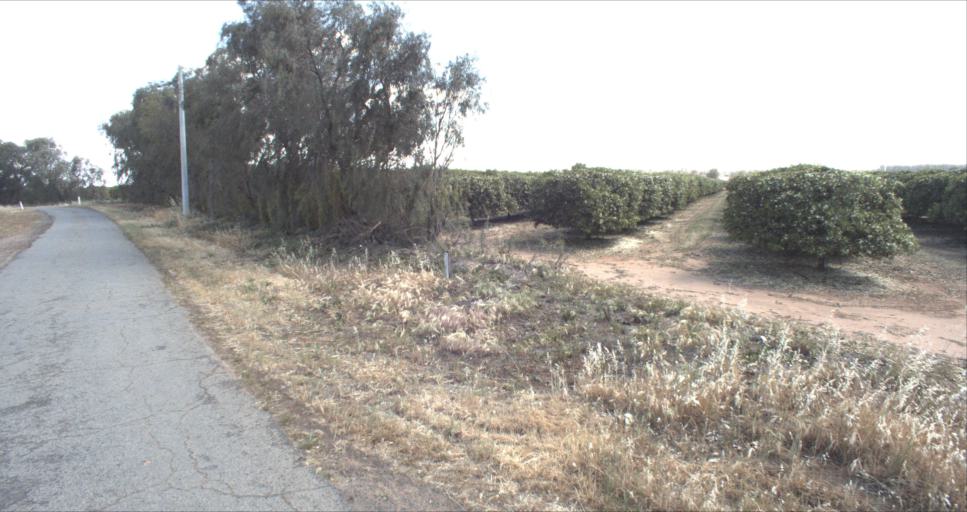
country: AU
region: New South Wales
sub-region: Leeton
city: Leeton
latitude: -34.5109
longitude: 146.2320
